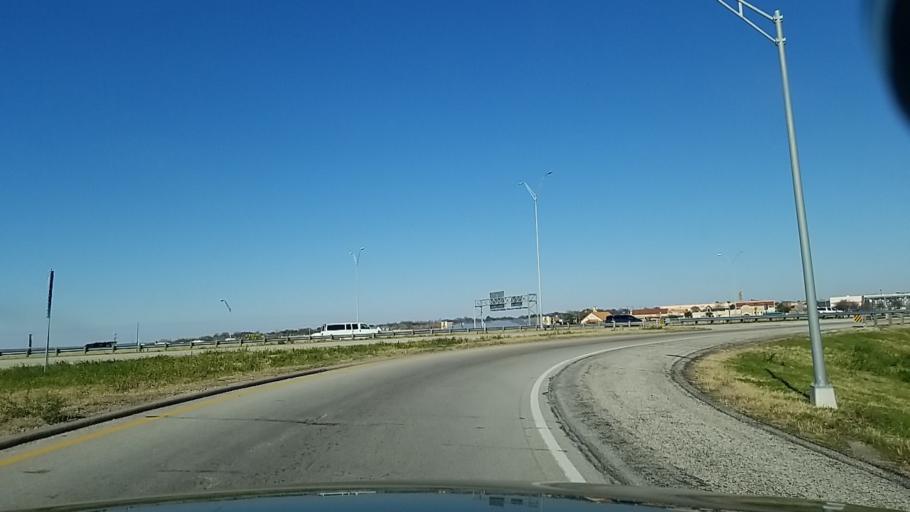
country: US
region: Texas
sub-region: Tarrant County
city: Sansom Park
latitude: 32.8073
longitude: -97.4189
